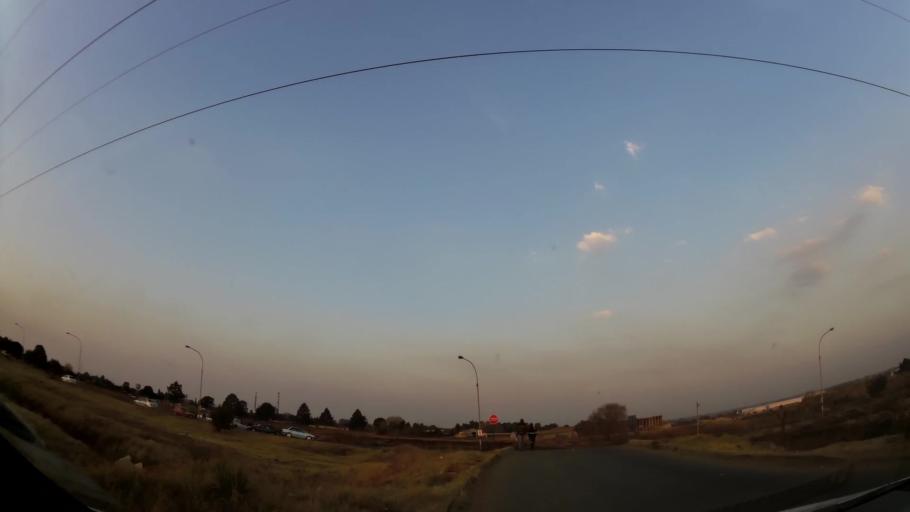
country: ZA
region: Gauteng
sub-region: Ekurhuleni Metropolitan Municipality
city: Springs
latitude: -26.2656
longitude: 28.3956
